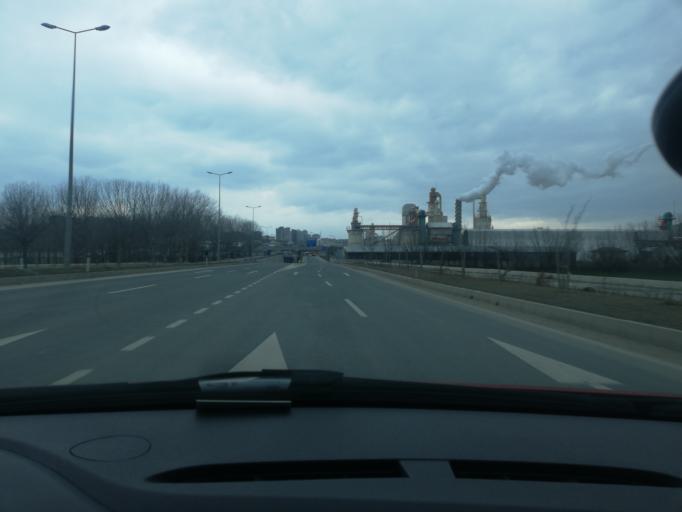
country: TR
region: Kastamonu
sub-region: Cide
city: Kastamonu
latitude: 41.4136
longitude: 33.8019
